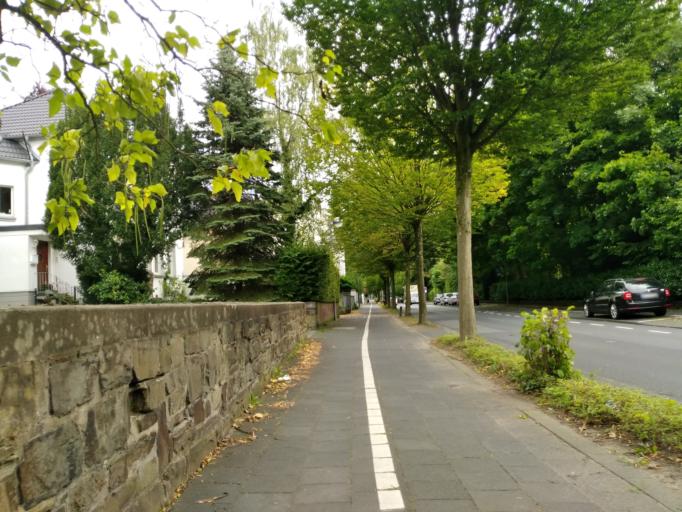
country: DE
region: North Rhine-Westphalia
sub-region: Regierungsbezirk Koln
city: Bad Honnef
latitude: 50.6541
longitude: 7.2170
